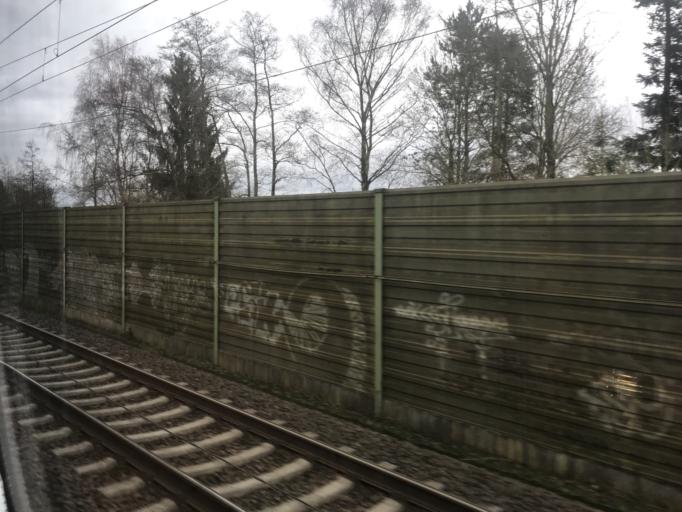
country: DE
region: Lower Saxony
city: Gifhorn
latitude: 52.4567
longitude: 10.5364
